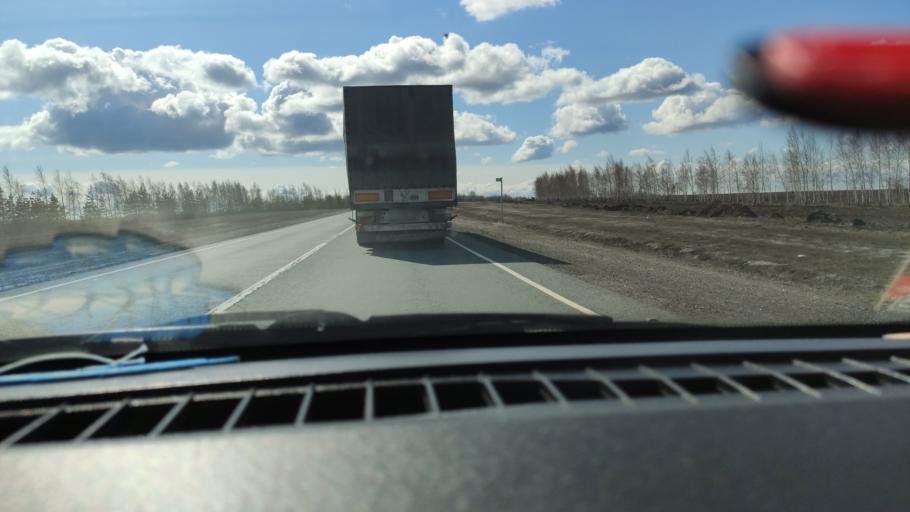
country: RU
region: Samara
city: Syzran'
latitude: 52.9345
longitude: 48.3079
